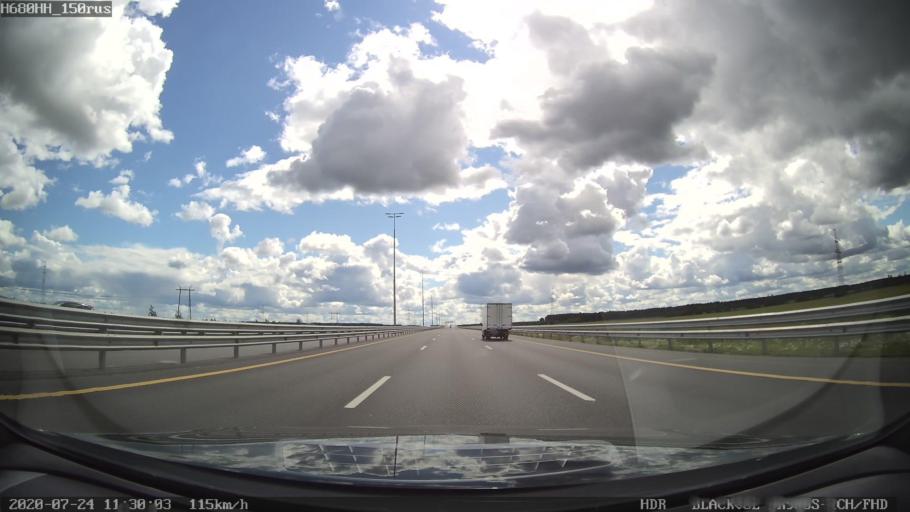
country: RU
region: Leningrad
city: Krasnyy Bor
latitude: 59.6740
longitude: 30.6044
